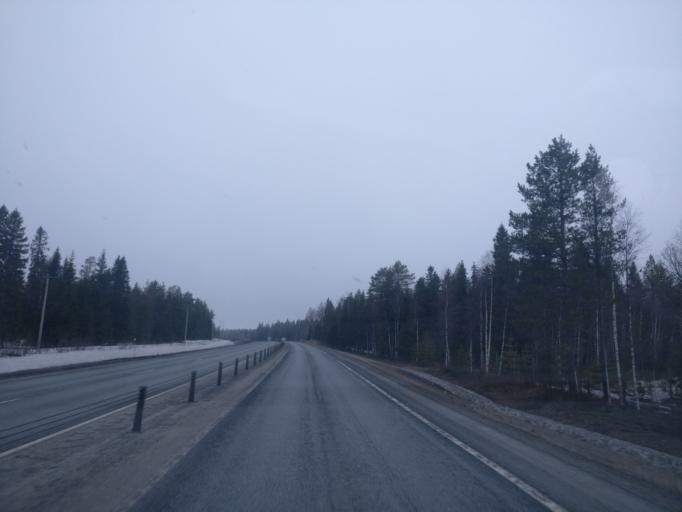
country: FI
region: Lapland
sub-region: Kemi-Tornio
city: Simo
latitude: 65.6685
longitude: 24.9641
